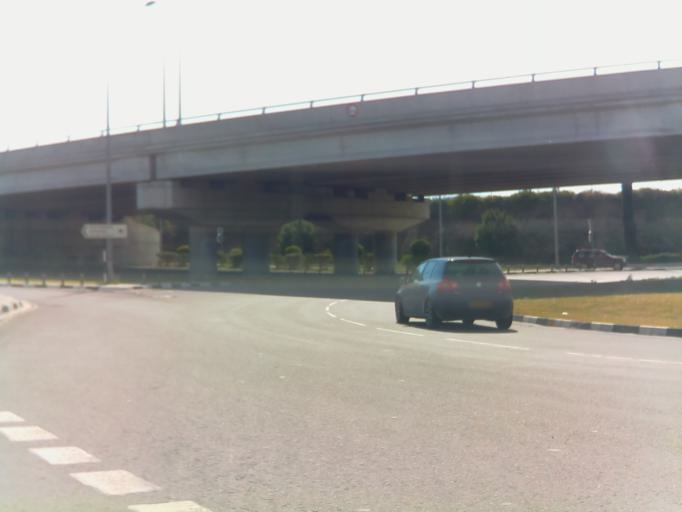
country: CY
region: Larnaka
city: Dhromolaxia
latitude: 34.8760
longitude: 33.6030
